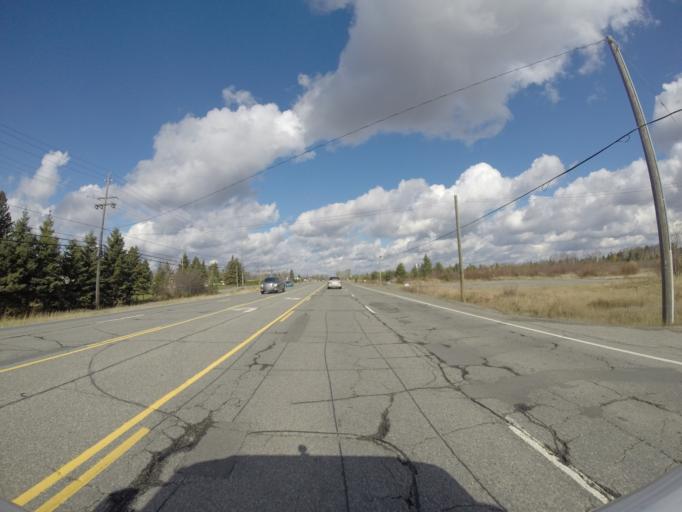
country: CA
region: Ontario
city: Greater Sudbury
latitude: 46.6244
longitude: -81.0076
